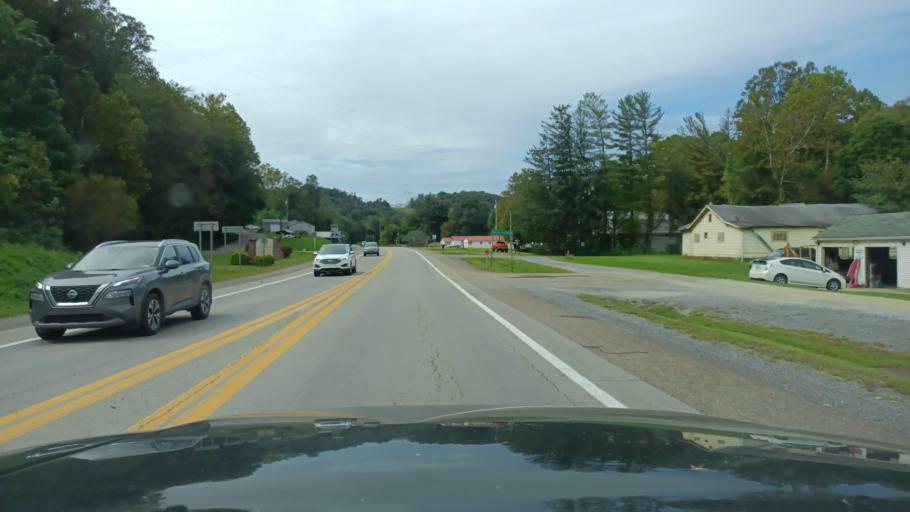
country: US
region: West Virginia
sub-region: Taylor County
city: Grafton
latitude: 39.3530
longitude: -80.0429
